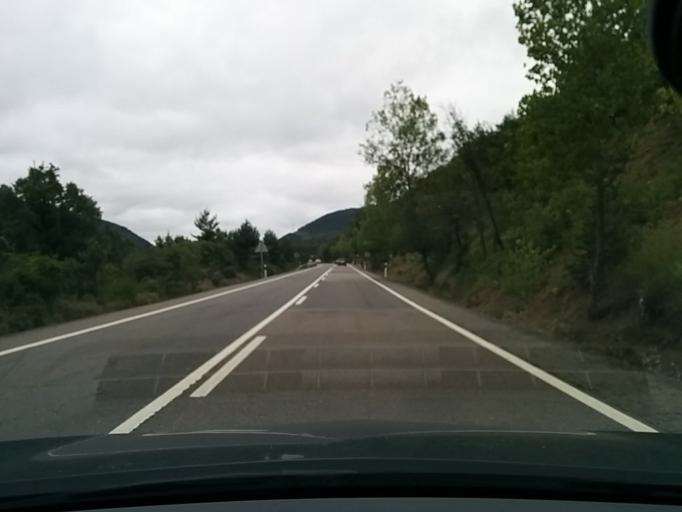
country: ES
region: Aragon
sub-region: Provincia de Huesca
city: Sabinanigo
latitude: 42.4758
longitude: -0.3798
